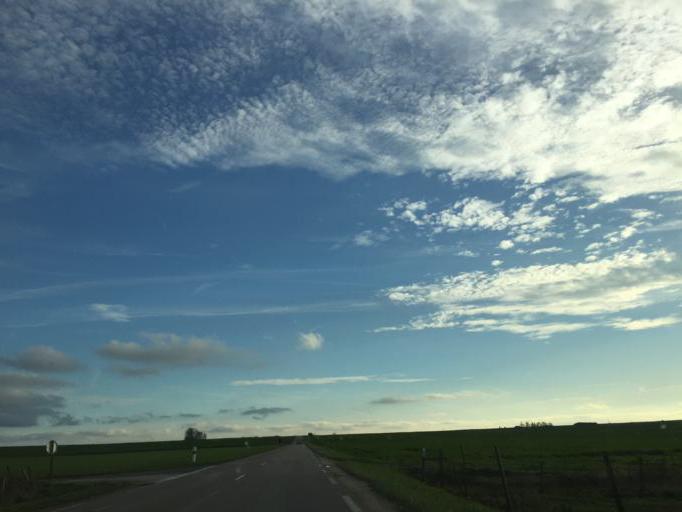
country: FR
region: Ile-de-France
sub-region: Departement de Seine-et-Marne
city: Jouy-le-Chatel
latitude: 48.6465
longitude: 3.1030
